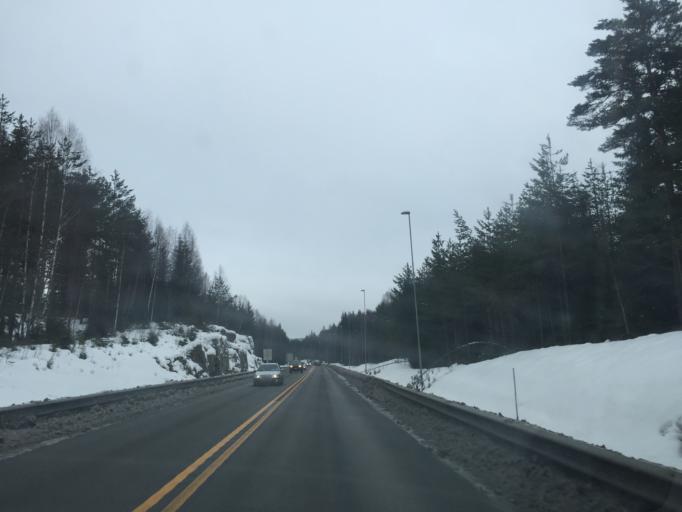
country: NO
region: Hedmark
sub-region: Stange
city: Stange
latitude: 60.7188
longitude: 11.2873
